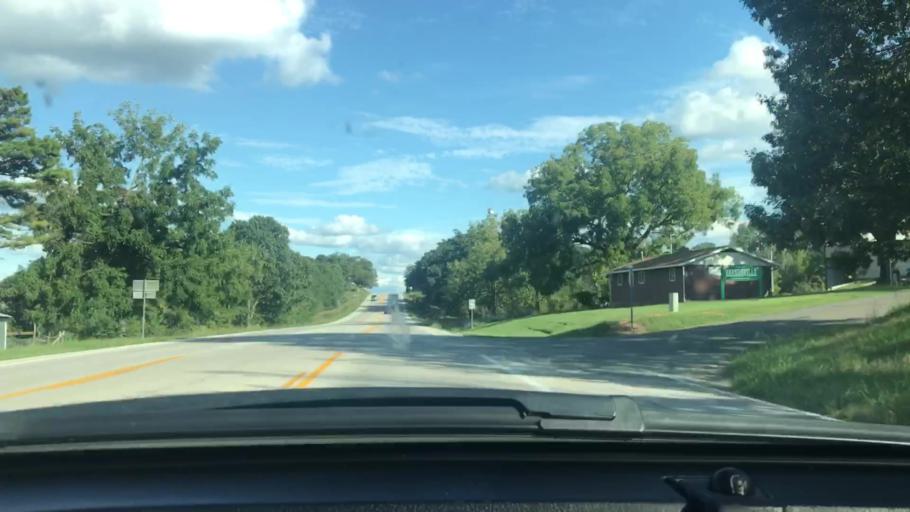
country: US
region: Missouri
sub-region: Howell County
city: West Plains
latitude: 36.6517
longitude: -91.6903
